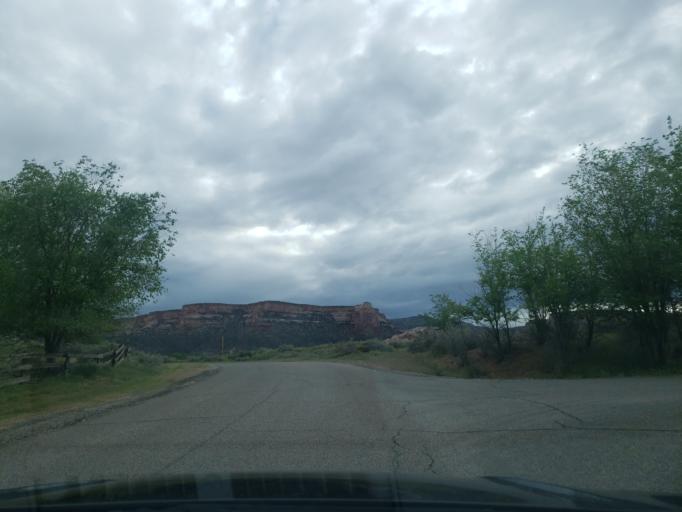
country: US
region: Colorado
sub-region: Mesa County
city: Redlands
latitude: 39.1031
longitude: -108.6801
